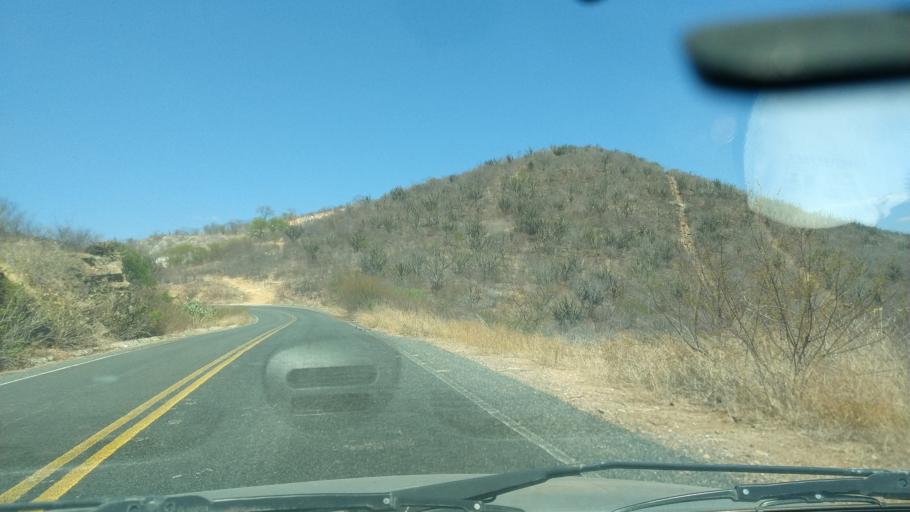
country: BR
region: Rio Grande do Norte
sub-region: Sao Tome
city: Sao Tome
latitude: -5.9679
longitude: -36.1560
